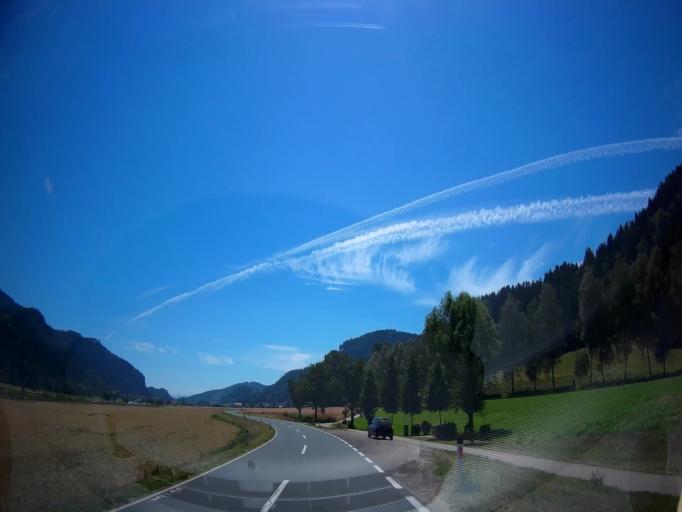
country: AT
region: Carinthia
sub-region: Politischer Bezirk Sankt Veit an der Glan
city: Micheldorf
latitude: 46.9255
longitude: 14.4277
